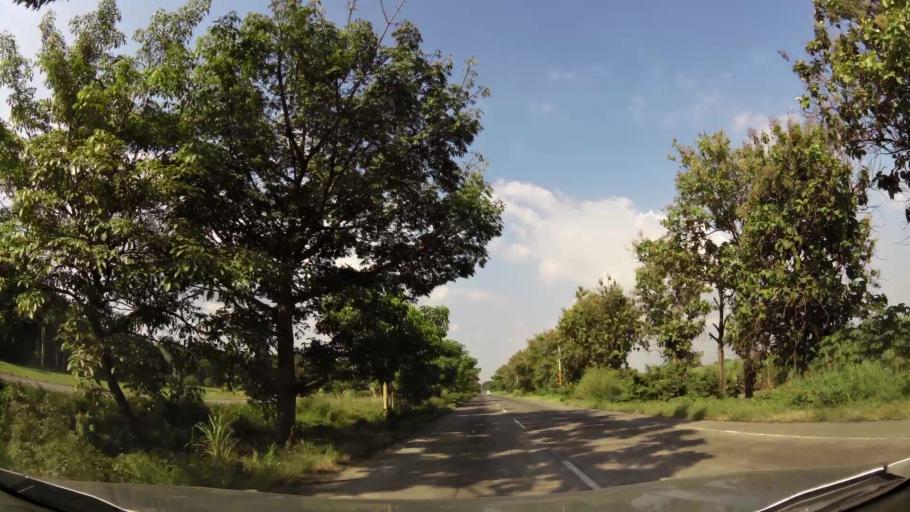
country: GT
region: Escuintla
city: Puerto San Jose
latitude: 14.0109
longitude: -90.7851
